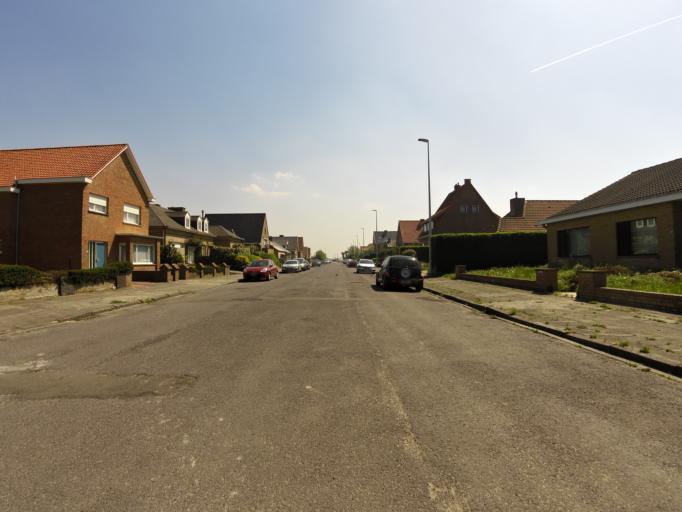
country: BE
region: Flanders
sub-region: Provincie West-Vlaanderen
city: Middelkerke
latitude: 51.2082
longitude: 2.8673
